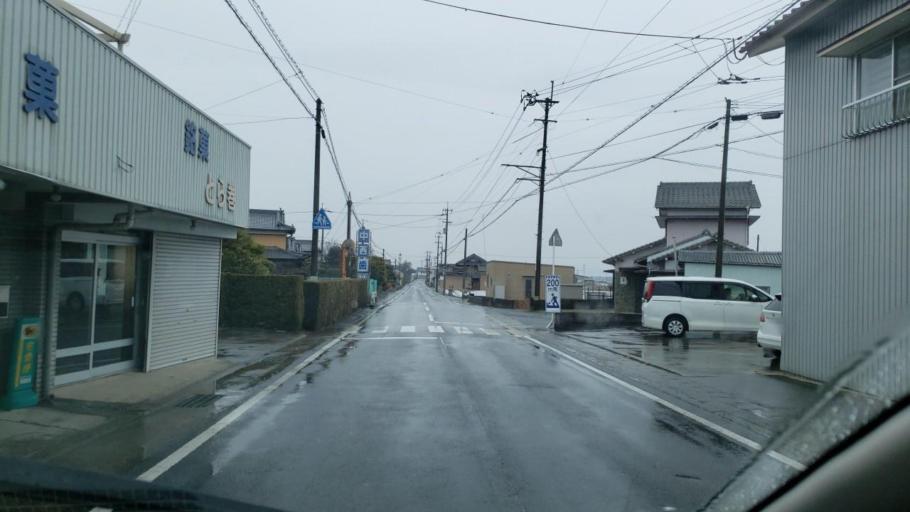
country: JP
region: Tokushima
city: Kamojimacho-jogejima
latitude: 34.0970
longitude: 134.3599
